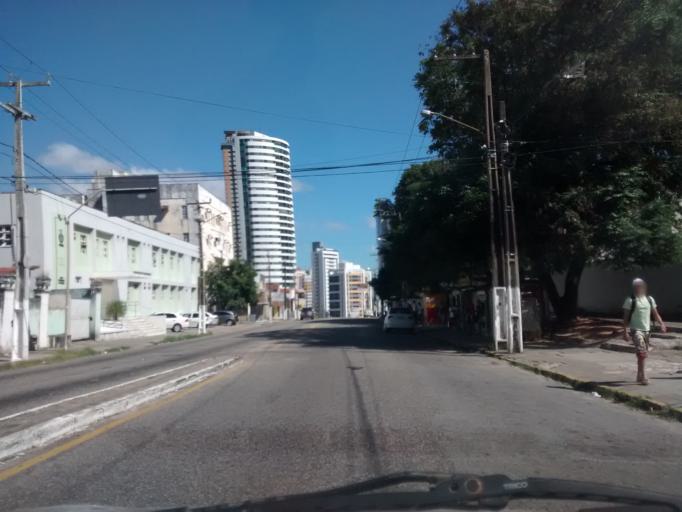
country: BR
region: Rio Grande do Norte
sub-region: Natal
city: Natal
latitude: -5.7813
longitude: -35.1977
